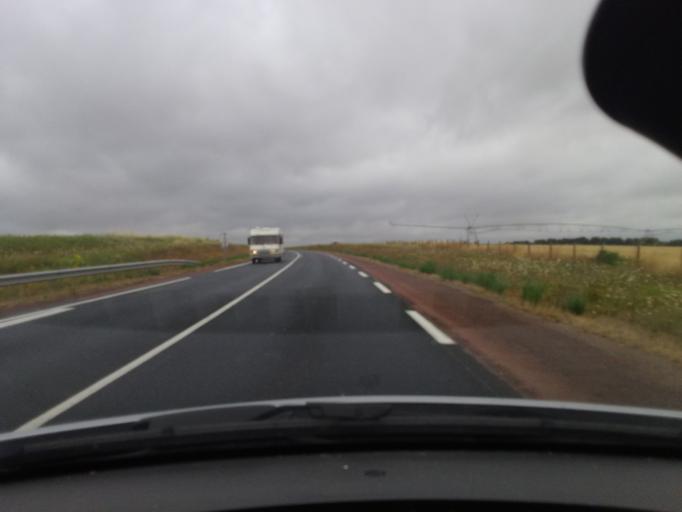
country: FR
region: Pays de la Loire
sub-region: Departement de la Vendee
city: Lucon
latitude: 46.4704
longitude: -1.1580
